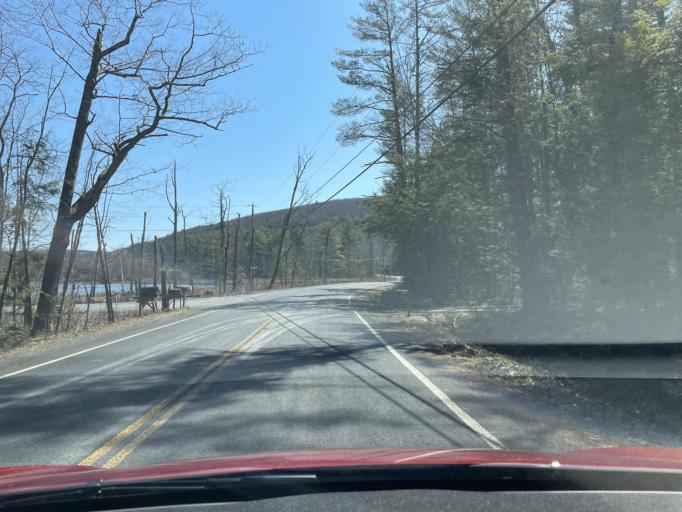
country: US
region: New York
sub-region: Ulster County
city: Shokan
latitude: 42.0203
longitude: -74.1897
